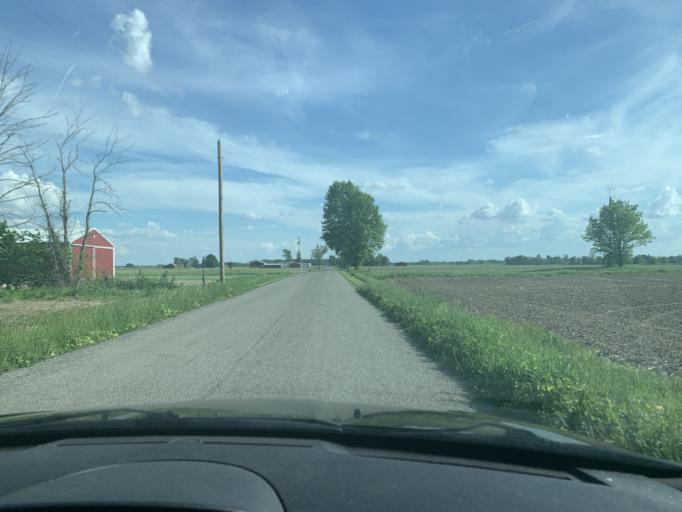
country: US
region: Ohio
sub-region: Logan County
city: De Graff
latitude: 40.2593
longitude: -84.0161
